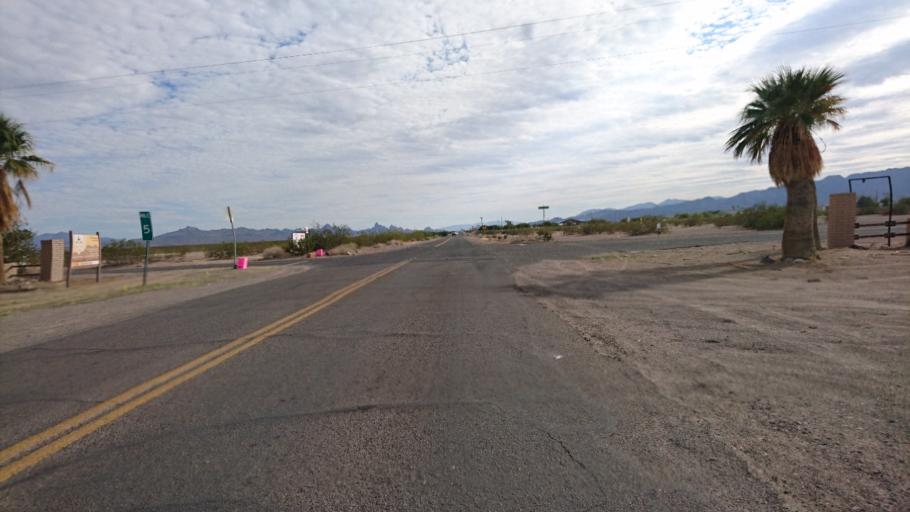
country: US
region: California
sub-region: San Bernardino County
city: Needles
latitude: 34.7793
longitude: -114.4807
